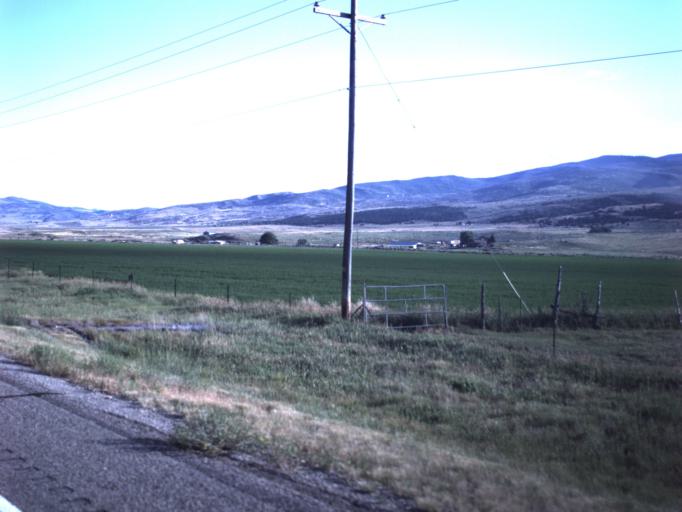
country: US
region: Utah
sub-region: Sanpete County
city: Fairview
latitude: 39.8088
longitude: -111.5048
